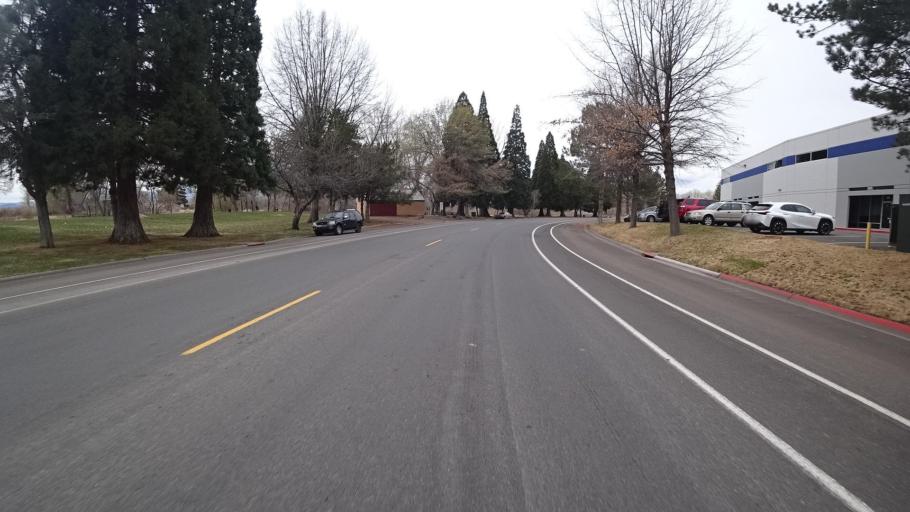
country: US
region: Nevada
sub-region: Washoe County
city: Sparks
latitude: 39.5128
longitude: -119.7313
